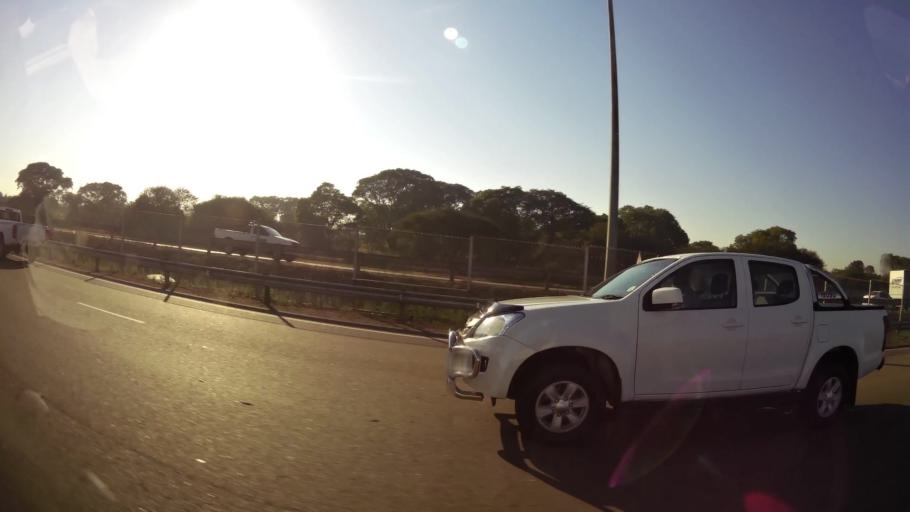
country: ZA
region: Gauteng
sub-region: City of Tshwane Metropolitan Municipality
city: Pretoria
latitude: -25.6689
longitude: 28.2725
